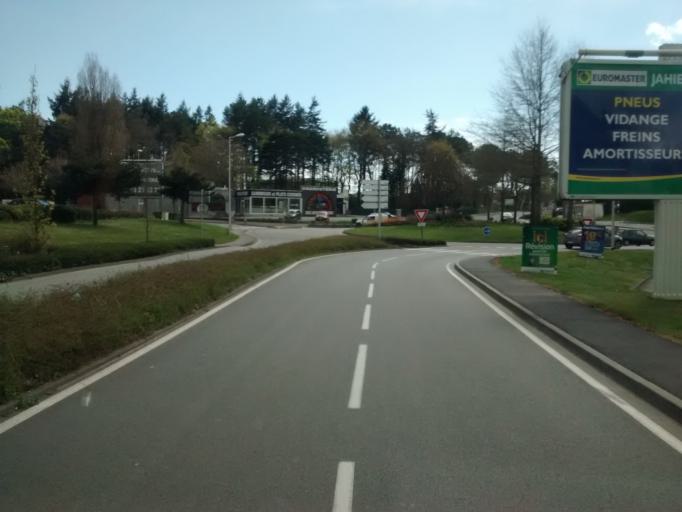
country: FR
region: Brittany
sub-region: Departement du Morbihan
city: Vannes
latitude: 47.6604
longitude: -2.7190
